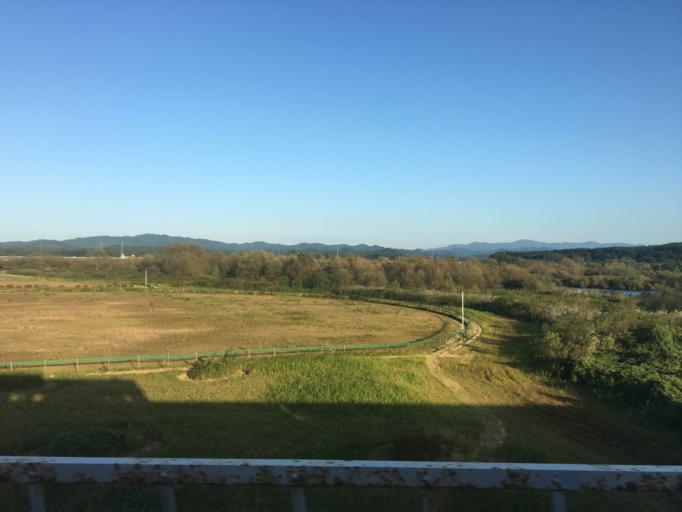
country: JP
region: Akita
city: Takanosu
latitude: 40.2134
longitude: 140.3541
